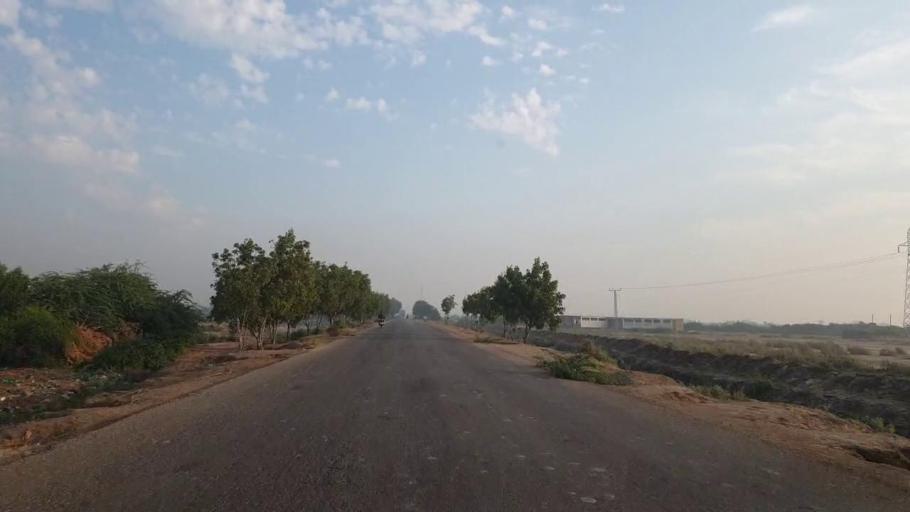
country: PK
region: Sindh
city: Badin
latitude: 24.6888
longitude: 68.9151
